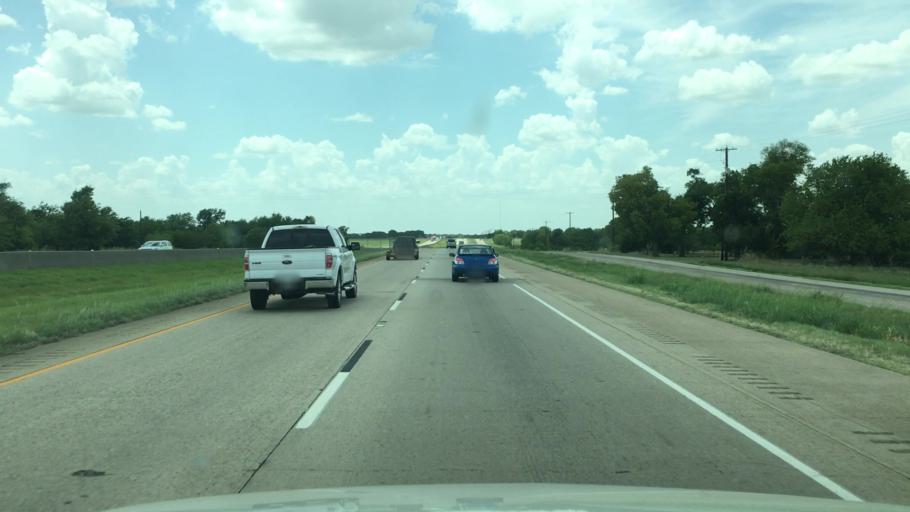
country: US
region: Texas
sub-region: Hopkins County
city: Sulphur Springs
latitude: 33.1209
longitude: -95.6889
